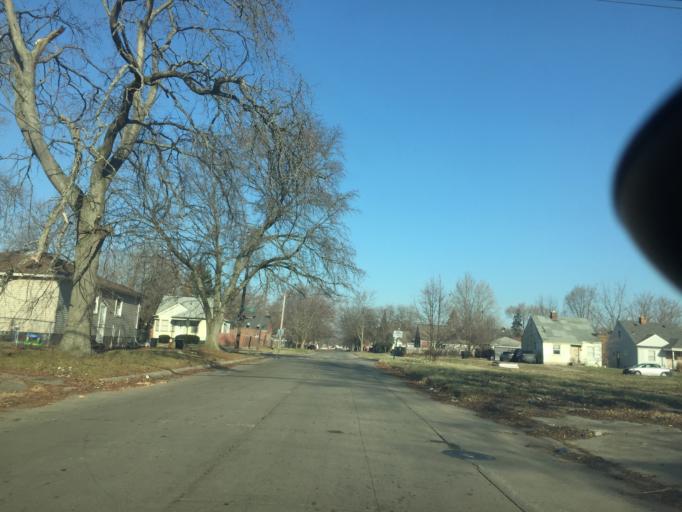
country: US
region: Michigan
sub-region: Macomb County
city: Eastpointe
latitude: 42.4452
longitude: -82.9560
